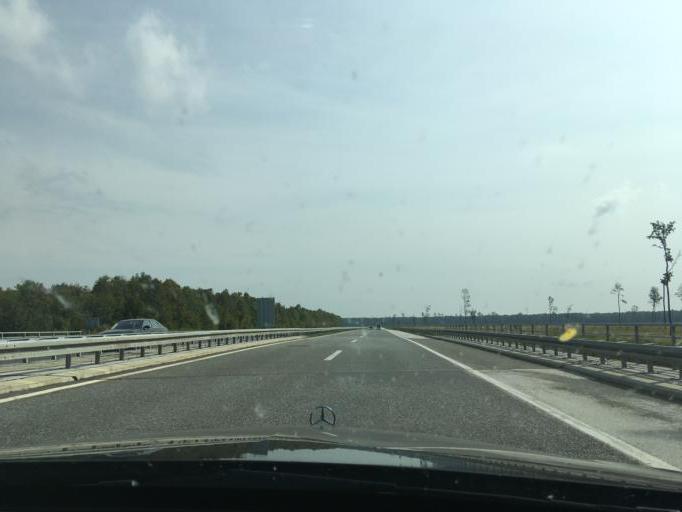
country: HR
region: Vukovarsko-Srijemska
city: Vrbanja
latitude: 45.0467
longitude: 18.9247
